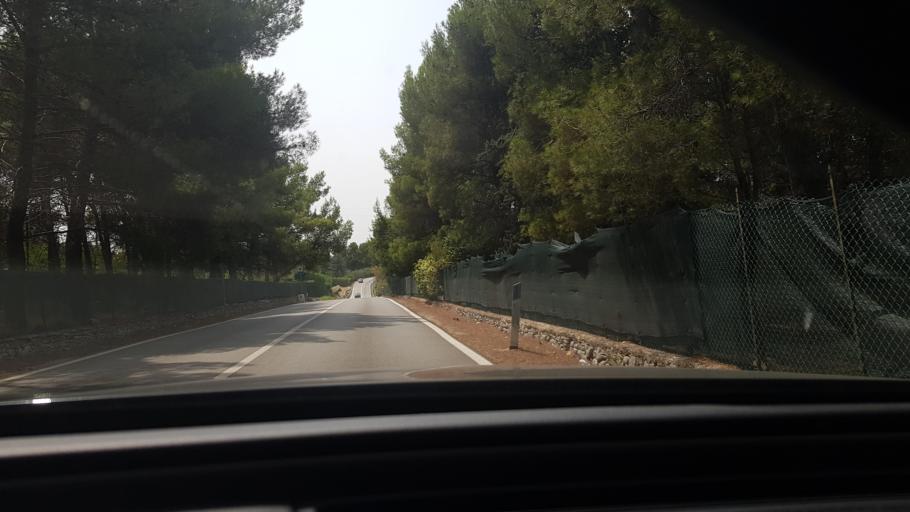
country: IT
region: Apulia
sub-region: Provincia di Barletta - Andria - Trani
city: Andria
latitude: 41.1262
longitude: 16.2877
